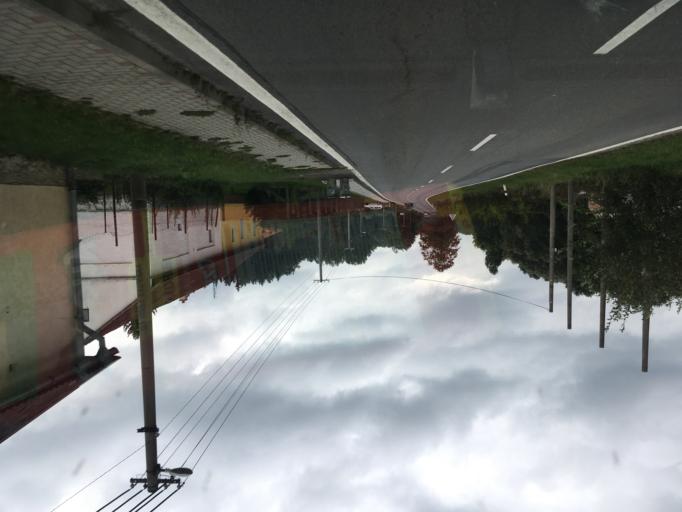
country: CZ
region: Vysocina
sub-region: Okres Pelhrimov
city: Pelhrimov
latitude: 49.3773
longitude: 15.2590
